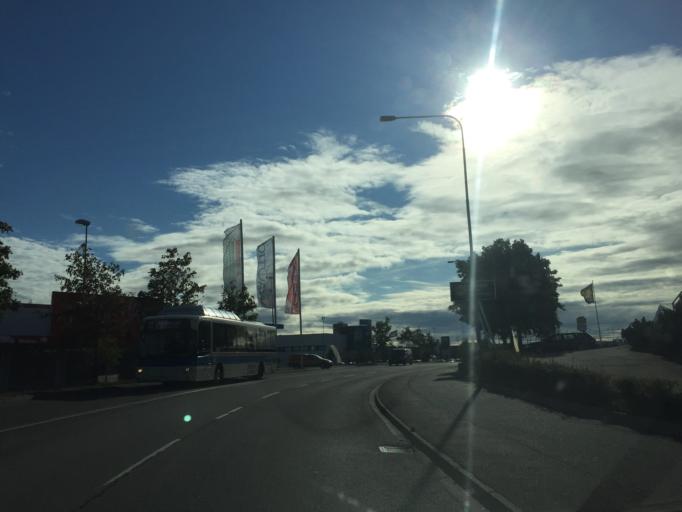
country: SE
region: Vaestmanland
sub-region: Vasteras
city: Vasteras
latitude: 59.6122
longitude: 16.4686
